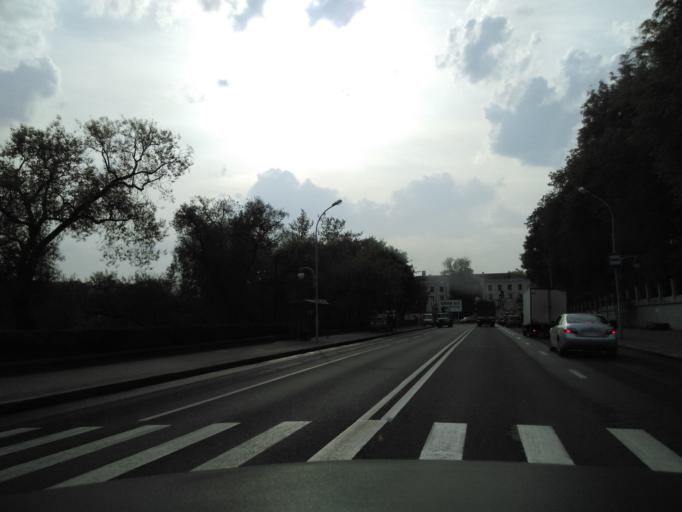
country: BY
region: Minsk
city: Minsk
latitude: 53.9002
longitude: 27.5708
